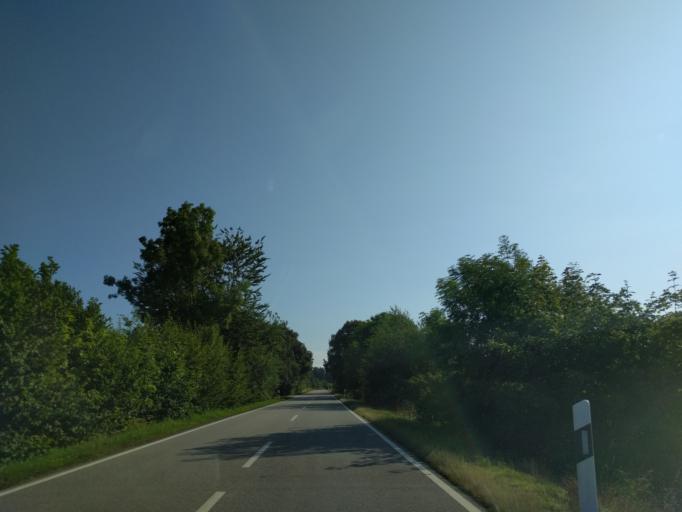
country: DE
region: Bavaria
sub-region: Lower Bavaria
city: Grafenau
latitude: 48.8506
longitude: 13.4388
